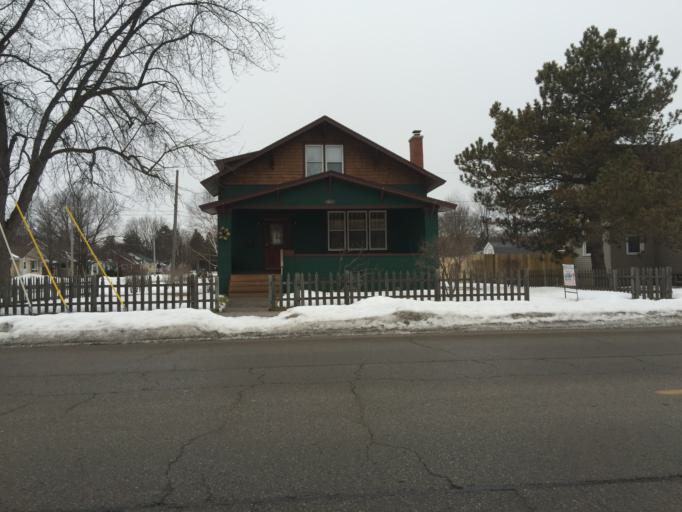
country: US
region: Wisconsin
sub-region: Marinette County
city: Marinette
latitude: 45.0872
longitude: -87.6295
